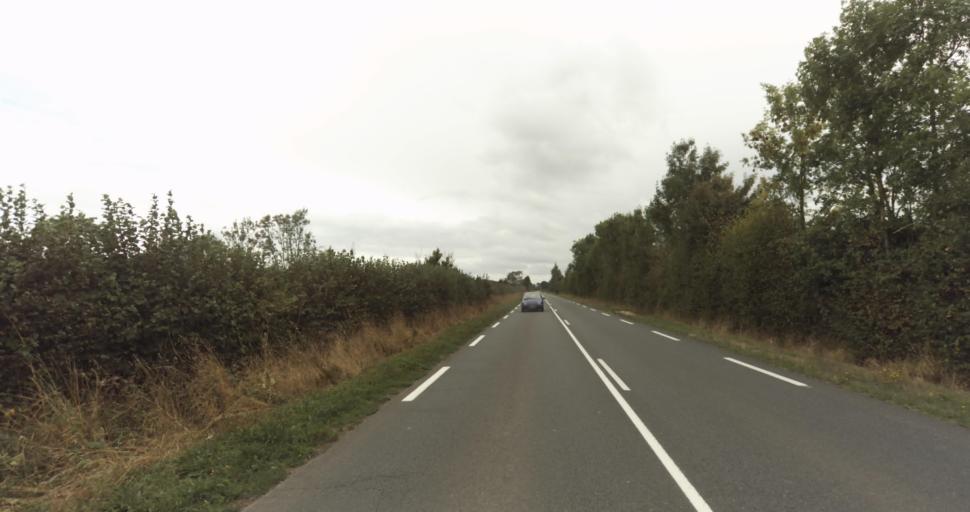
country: FR
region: Lower Normandy
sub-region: Departement de l'Orne
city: Vimoutiers
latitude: 48.8766
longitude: 0.2558
